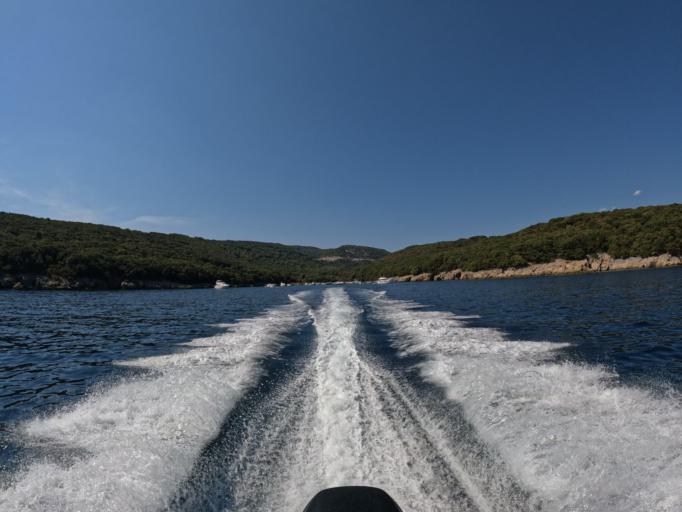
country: HR
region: Primorsko-Goranska
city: Cres
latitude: 44.9490
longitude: 14.4647
